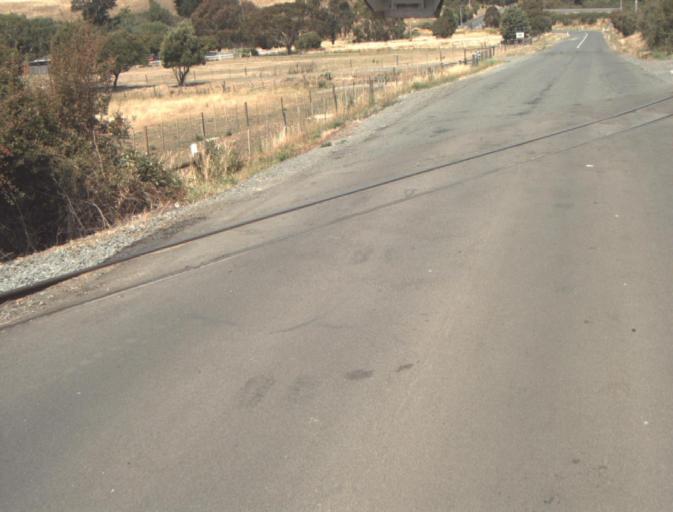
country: AU
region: Tasmania
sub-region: Launceston
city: Newstead
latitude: -41.4662
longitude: 147.1856
